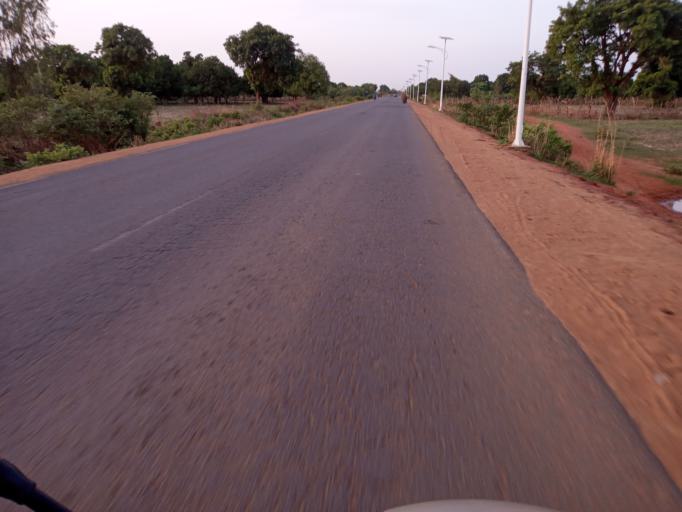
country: ML
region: Bamako
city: Bamako
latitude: 12.3017
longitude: -8.1579
